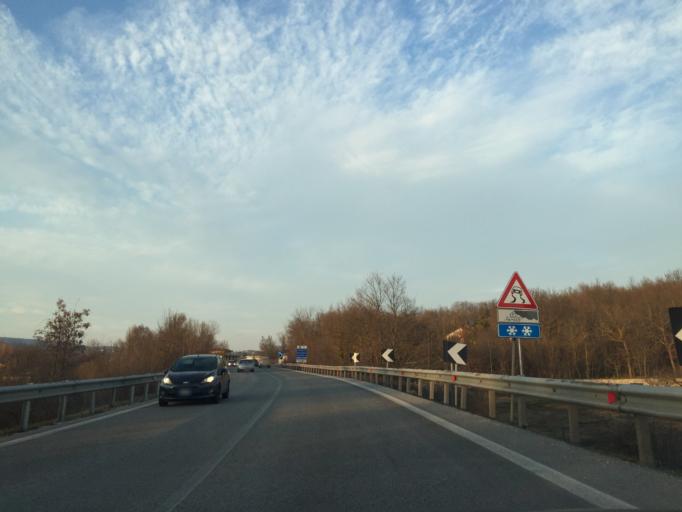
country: IT
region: Molise
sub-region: Provincia di Campobasso
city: Vinchiaturo
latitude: 41.4822
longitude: 14.5886
